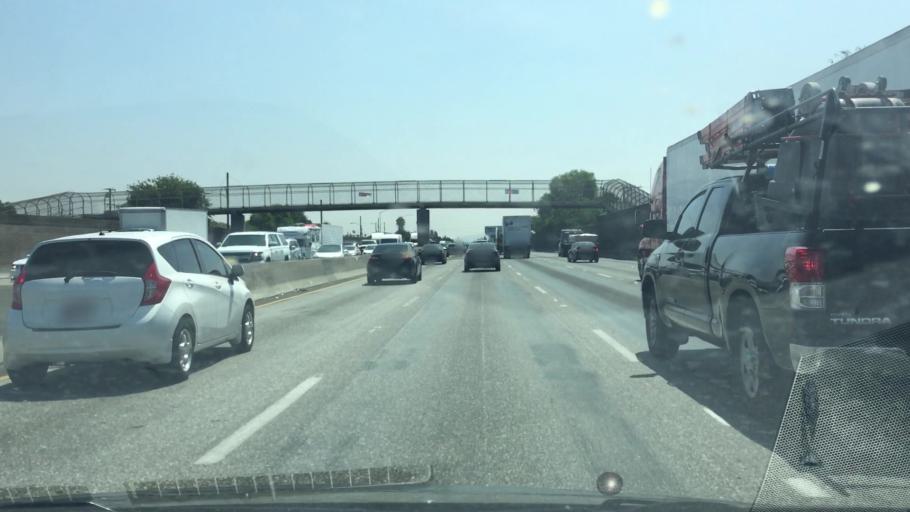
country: US
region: California
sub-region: Los Angeles County
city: East Los Angeles
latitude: 34.0200
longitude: -118.1865
